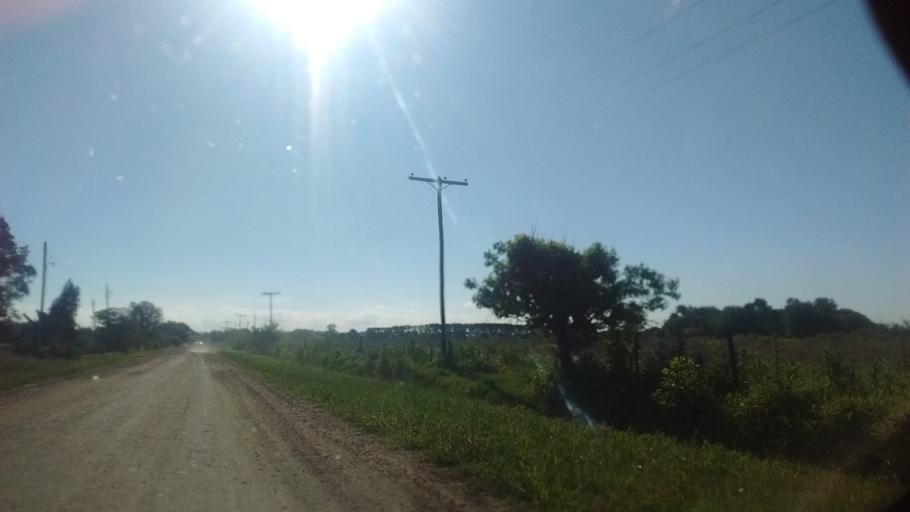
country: AR
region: Santa Fe
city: Funes
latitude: -32.8608
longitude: -60.7984
